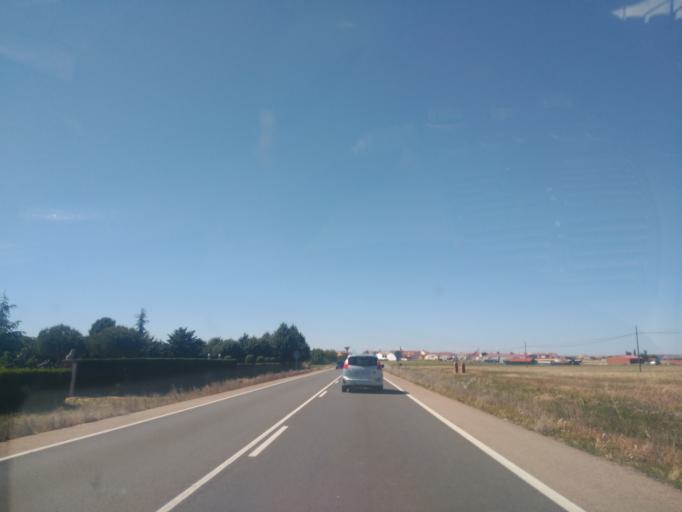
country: ES
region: Castille and Leon
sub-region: Provincia de Salamanca
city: Calvarrasa de Arriba
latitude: 40.8986
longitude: -5.5890
